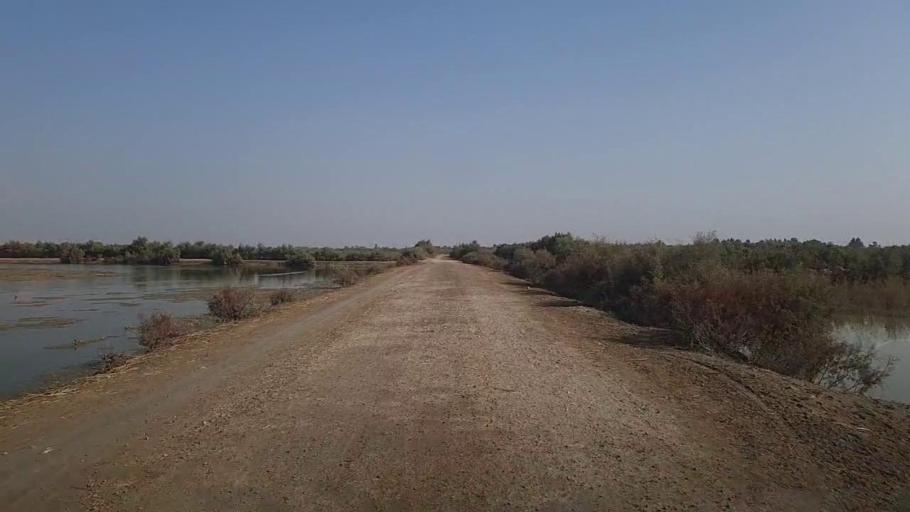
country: PK
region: Sindh
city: Kandhkot
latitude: 28.3589
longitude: 69.3308
